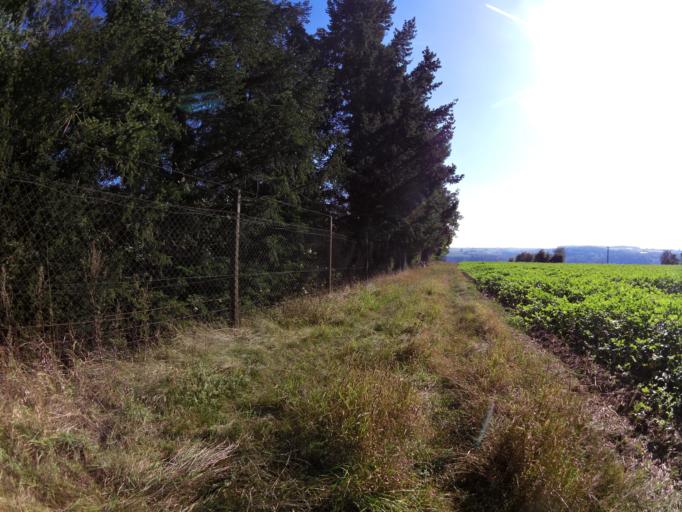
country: DE
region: Bavaria
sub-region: Regierungsbezirk Unterfranken
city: Ochsenfurt
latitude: 49.6755
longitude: 10.0623
